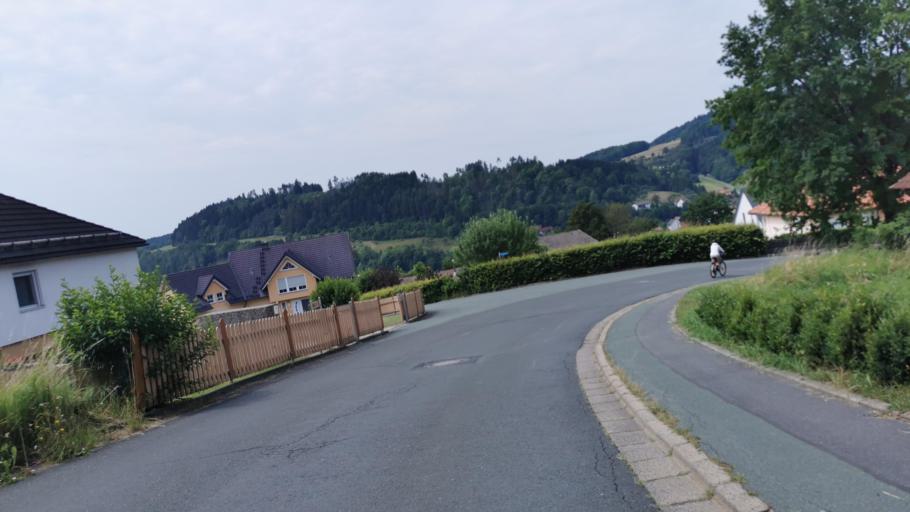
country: DE
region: Bavaria
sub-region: Upper Franconia
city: Marktrodach
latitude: 50.2768
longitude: 11.3720
